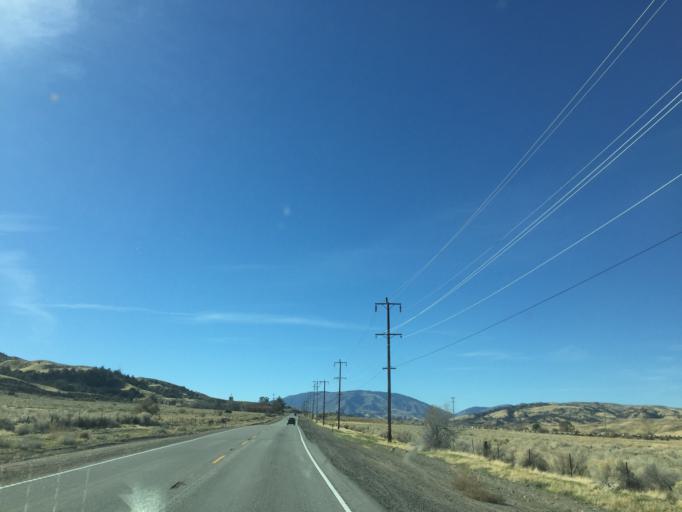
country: US
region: California
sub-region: Kern County
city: Lebec
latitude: 34.7649
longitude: -118.7180
